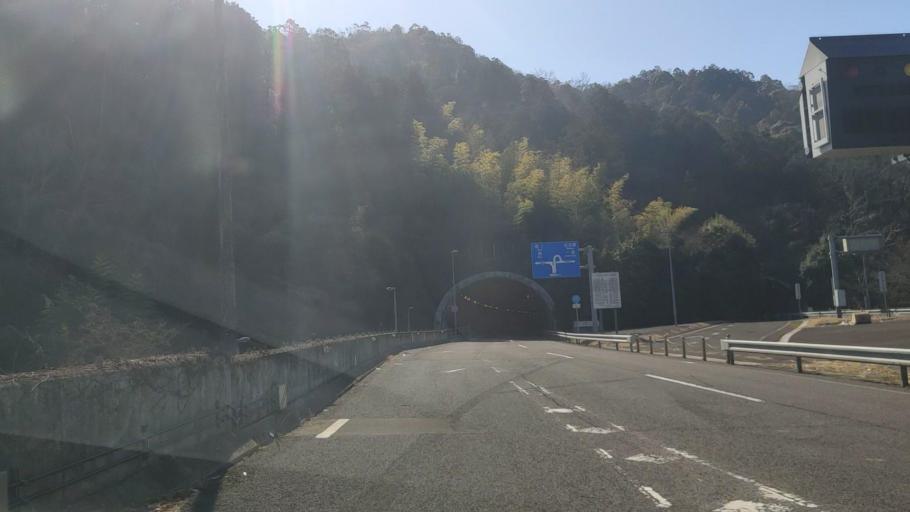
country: JP
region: Gifu
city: Gifu-shi
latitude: 35.4364
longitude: 136.7976
